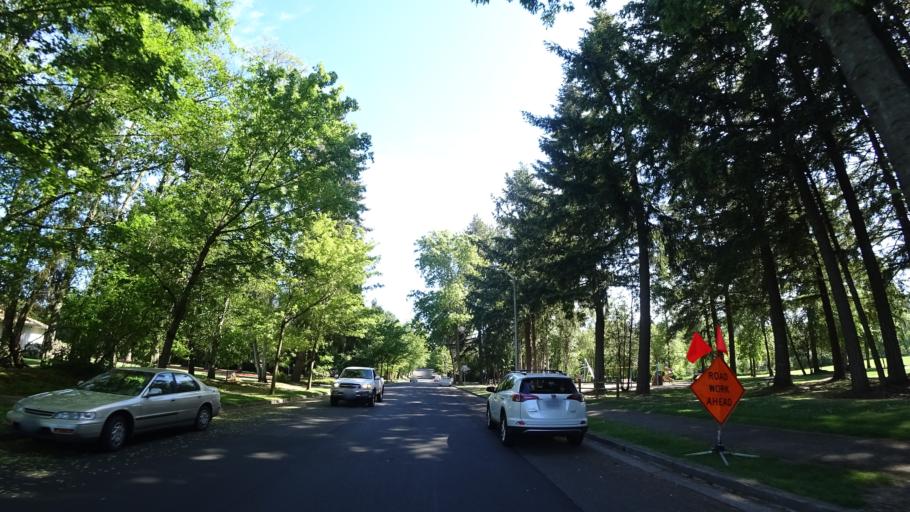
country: US
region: Oregon
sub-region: Washington County
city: Beaverton
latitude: 45.4544
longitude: -122.8157
